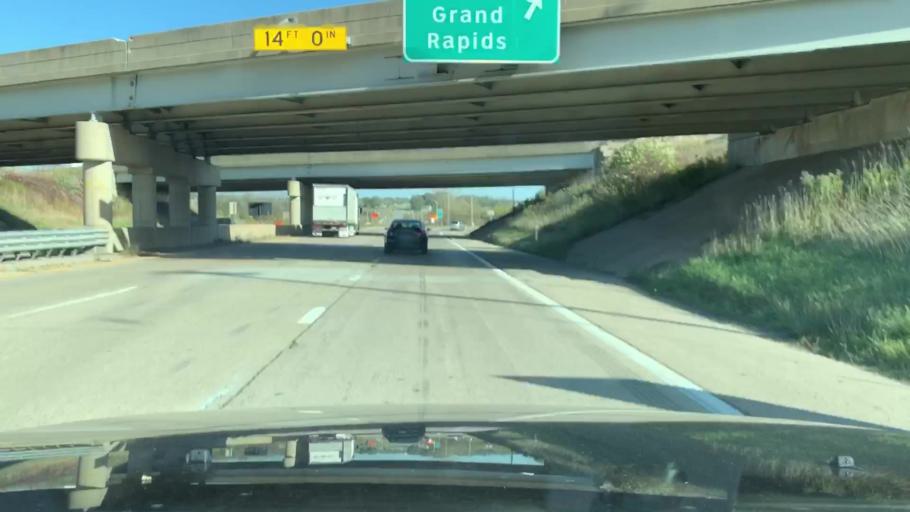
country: US
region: Michigan
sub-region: Ottawa County
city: Zeeland
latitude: 42.8121
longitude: -85.9818
